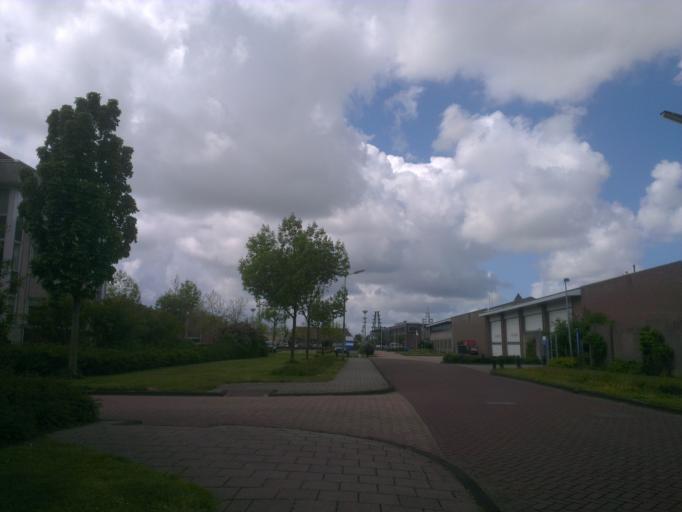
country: NL
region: North Holland
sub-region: Gemeente Langedijk
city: Broek op Langedijk
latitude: 52.6870
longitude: 4.8054
